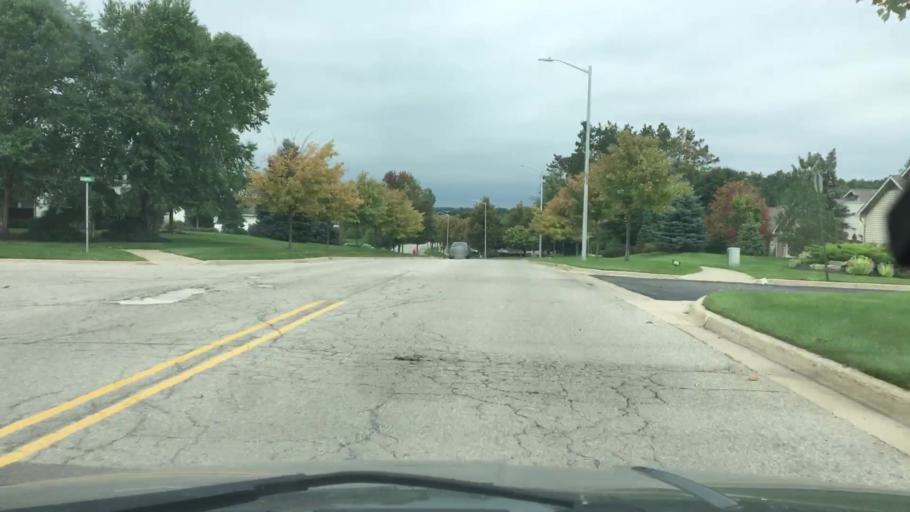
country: US
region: Michigan
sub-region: Livingston County
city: Brighton
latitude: 42.5108
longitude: -83.7834
